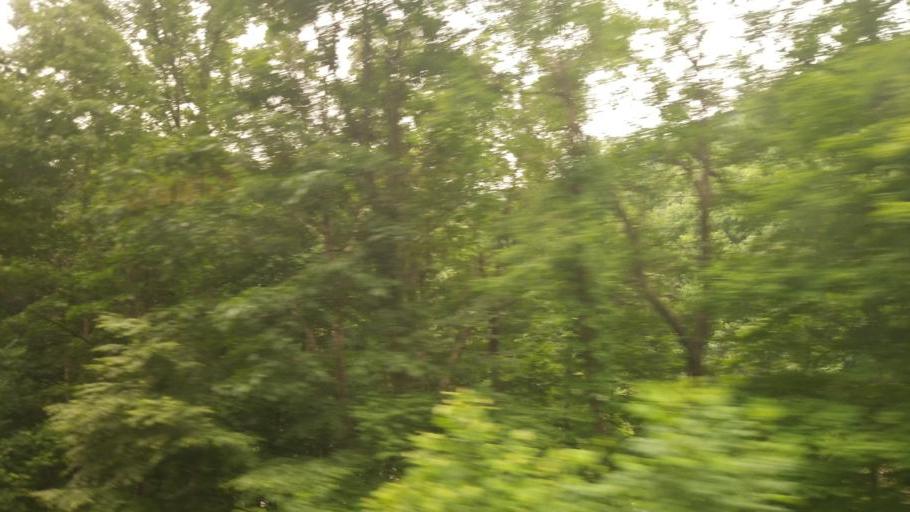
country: US
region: Pennsylvania
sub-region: Fayette County
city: South Connellsville
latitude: 39.9208
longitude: -79.4738
